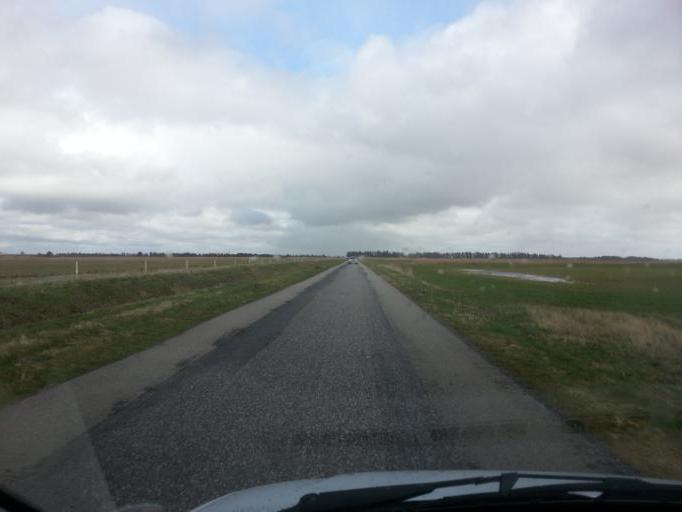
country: DK
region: Central Jutland
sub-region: Ringkobing-Skjern Kommune
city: Ringkobing
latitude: 56.2041
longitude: 8.1421
